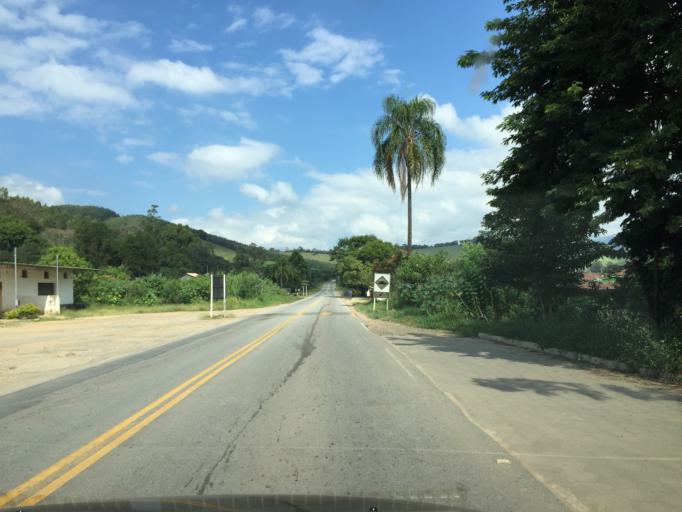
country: BR
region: Minas Gerais
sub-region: Passa Quatro
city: Passa Quatro
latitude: -22.3578
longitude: -44.9512
